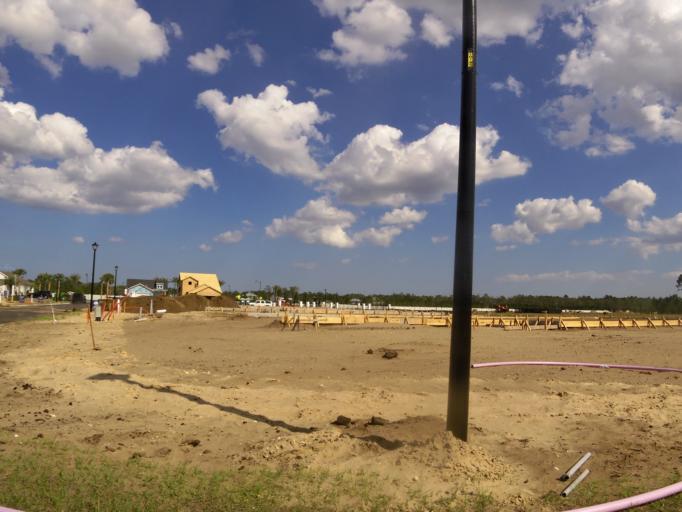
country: US
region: Florida
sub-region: Saint Johns County
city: Palm Valley
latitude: 30.1914
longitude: -81.5073
